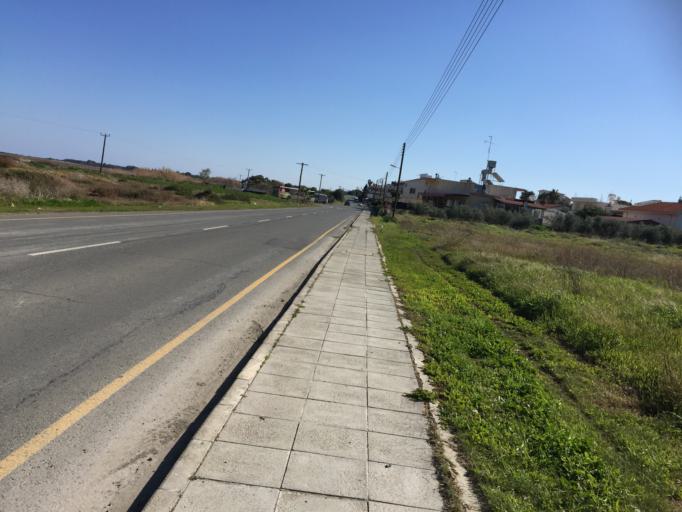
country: CY
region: Larnaka
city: Kolossi
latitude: 34.6040
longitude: 32.9533
